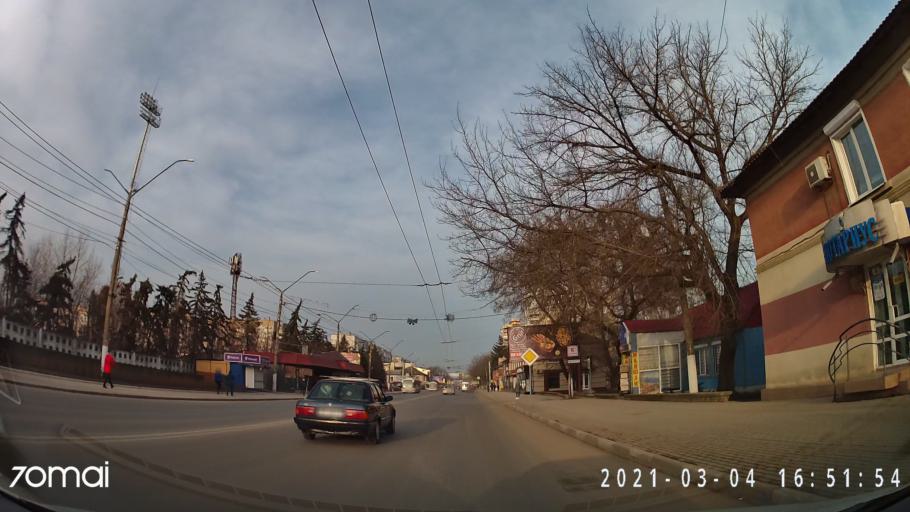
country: MD
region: Balti
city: Balti
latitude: 47.7649
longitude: 27.9332
